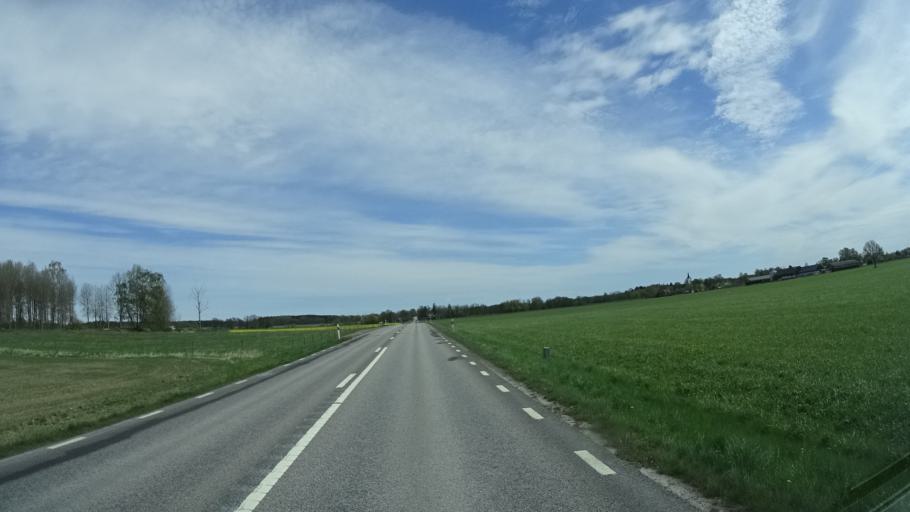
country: SE
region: OEstergoetland
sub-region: Linkopings Kommun
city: Vikingstad
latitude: 58.3701
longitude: 15.3588
